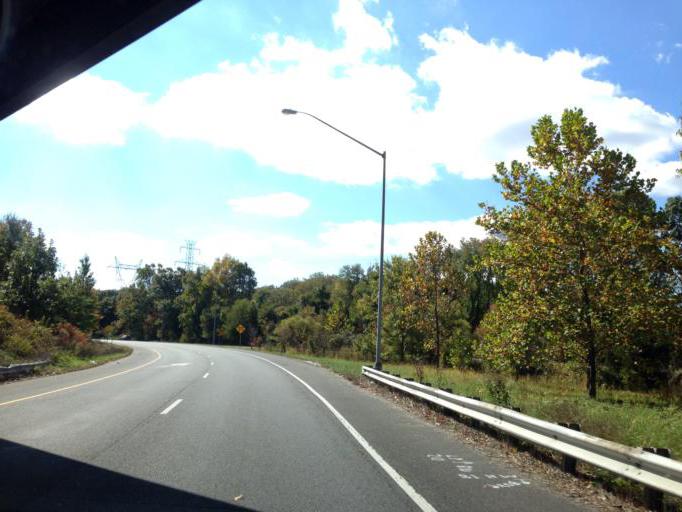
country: US
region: Maryland
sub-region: Howard County
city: Ellicott City
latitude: 39.2741
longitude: -76.8182
